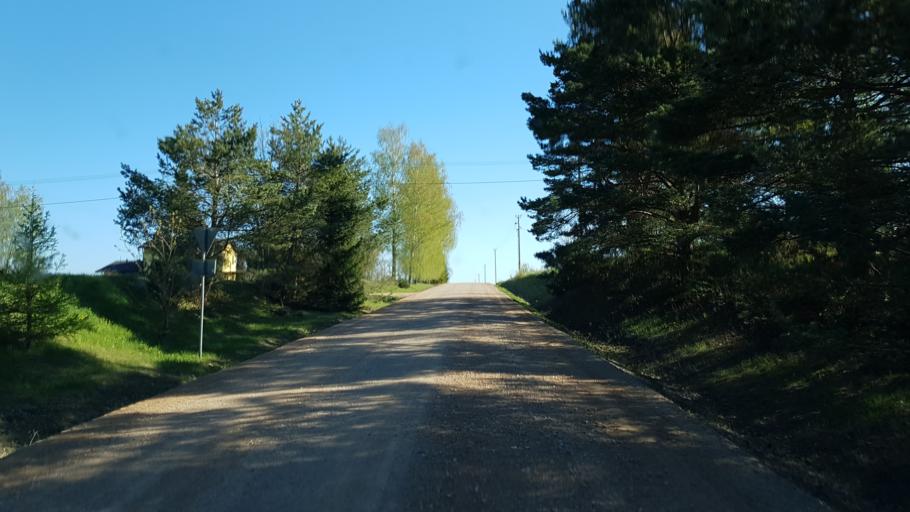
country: EE
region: Polvamaa
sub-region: Polva linn
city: Polva
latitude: 58.0945
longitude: 27.2203
